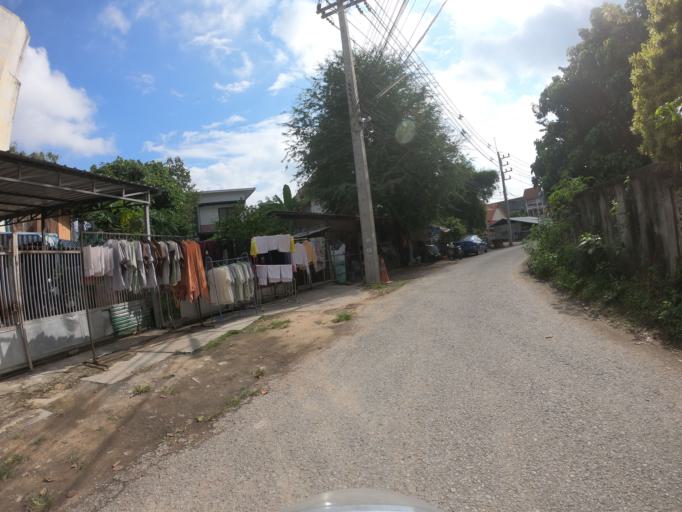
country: TH
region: Chiang Mai
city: Chiang Mai
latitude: 18.8130
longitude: 98.9820
